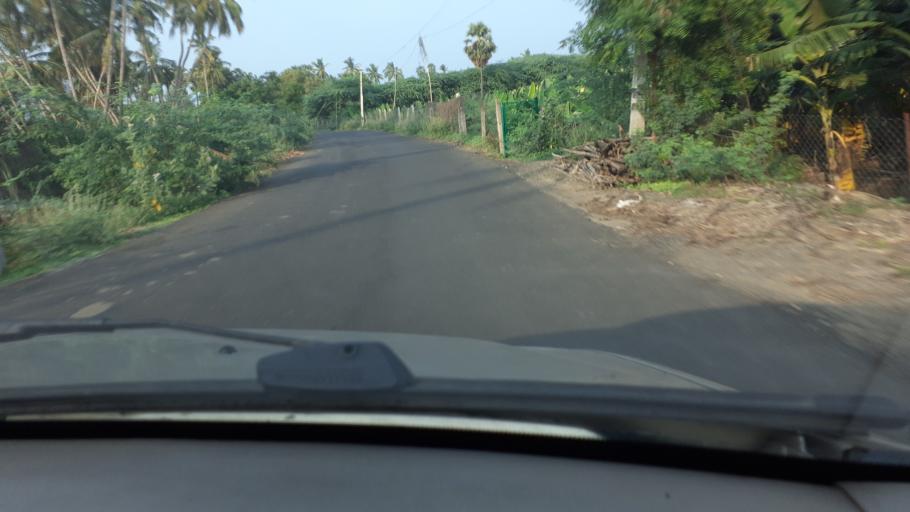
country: IN
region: Tamil Nadu
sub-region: Thoothukkudi
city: Alwar Tirunagari
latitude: 8.6004
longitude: 77.9754
